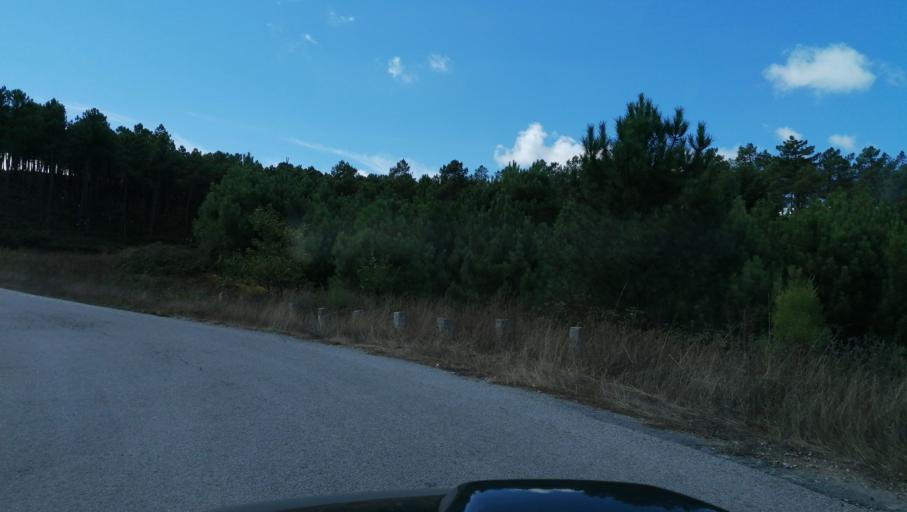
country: PT
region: Vila Real
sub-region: Vila Pouca de Aguiar
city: Vila Pouca de Aguiar
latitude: 41.5562
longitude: -7.6288
